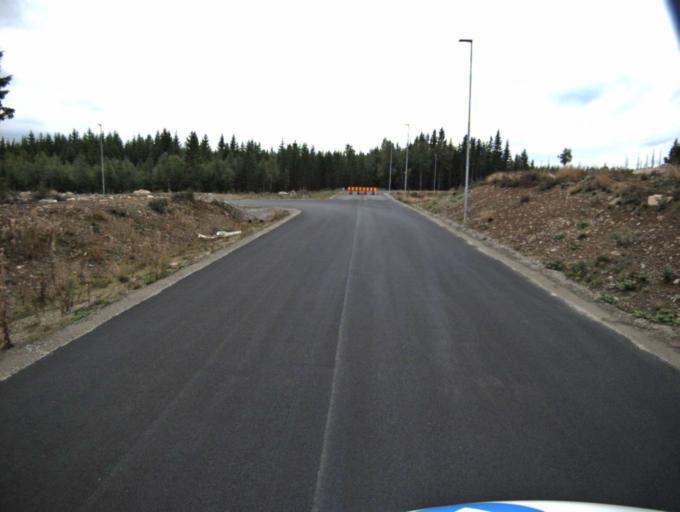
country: SE
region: Vaestra Goetaland
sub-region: Ulricehamns Kommun
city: Ulricehamn
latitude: 57.8025
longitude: 13.4659
